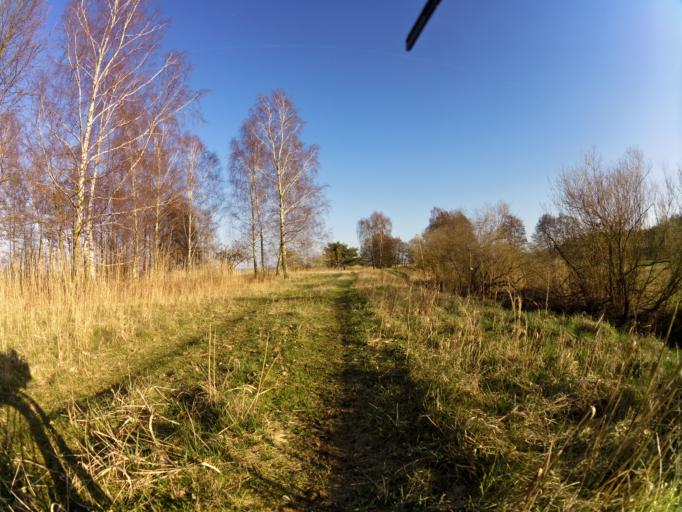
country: PL
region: West Pomeranian Voivodeship
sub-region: Powiat policki
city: Nowe Warpno
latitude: 53.7202
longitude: 14.3390
